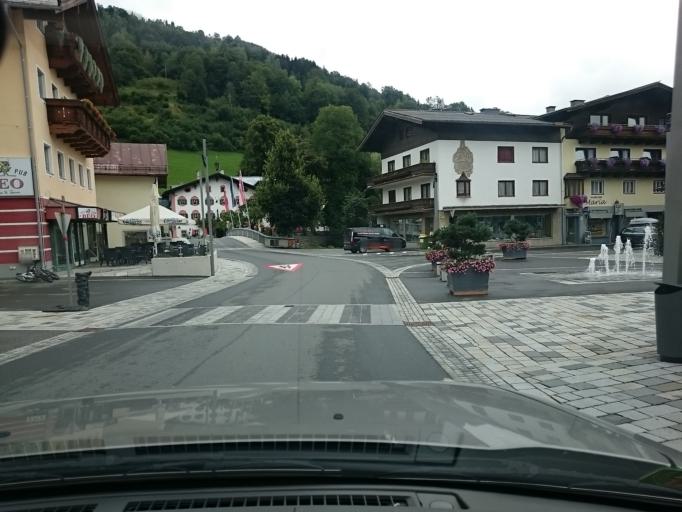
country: AT
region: Salzburg
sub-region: Politischer Bezirk Zell am See
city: Bruck an der Grossglocknerstrasse
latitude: 47.2866
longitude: 12.8238
